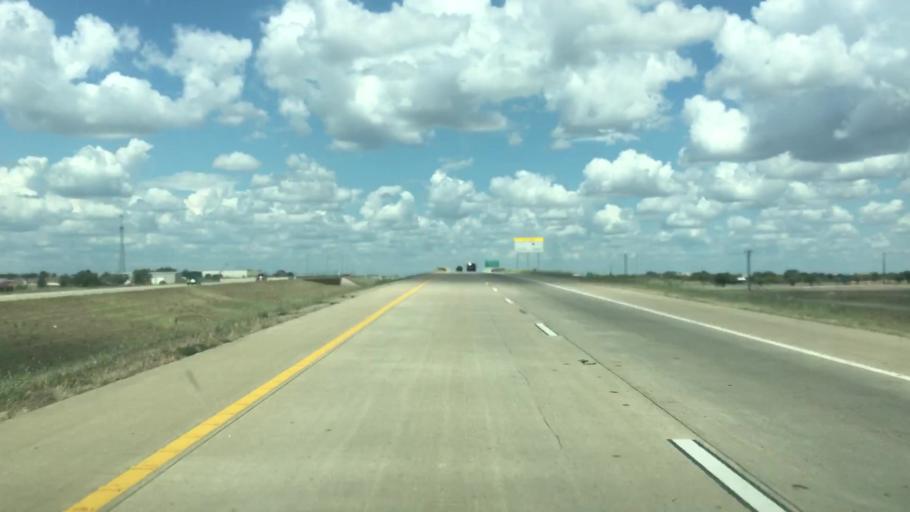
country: US
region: Texas
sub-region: Williamson County
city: Hutto
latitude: 30.5735
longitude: -97.5835
